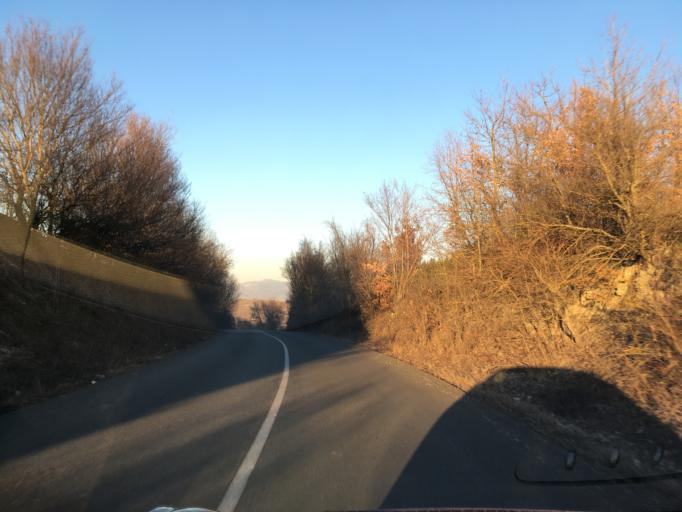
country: GR
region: West Macedonia
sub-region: Nomos Kozanis
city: Koila
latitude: 40.3253
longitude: 21.7993
